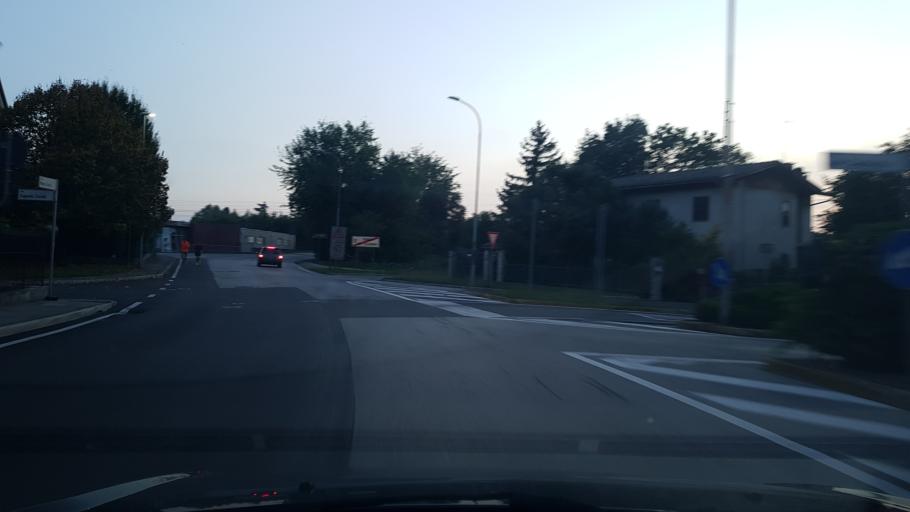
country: IT
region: Friuli Venezia Giulia
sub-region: Provincia di Gorizia
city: Ronchi dei Legionari
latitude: 45.8236
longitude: 13.5145
